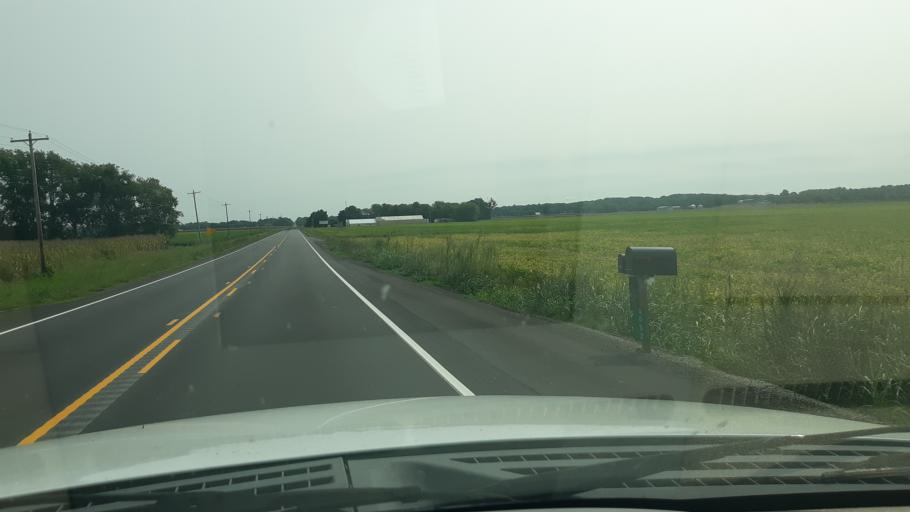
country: US
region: Indiana
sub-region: Gibson County
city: Princeton
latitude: 38.3558
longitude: -87.6520
